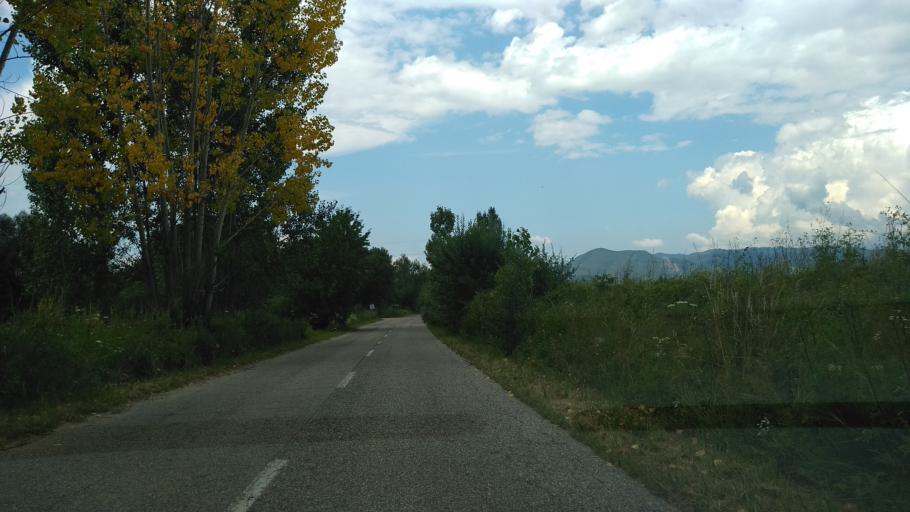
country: RO
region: Hunedoara
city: Salasu de Sus
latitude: 45.5002
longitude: 22.9483
